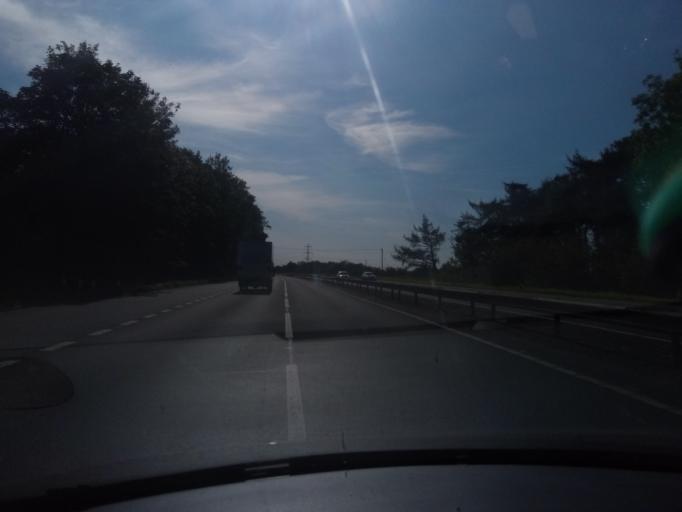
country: GB
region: England
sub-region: North Yorkshire
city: Thirsk
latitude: 54.2780
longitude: -1.3417
